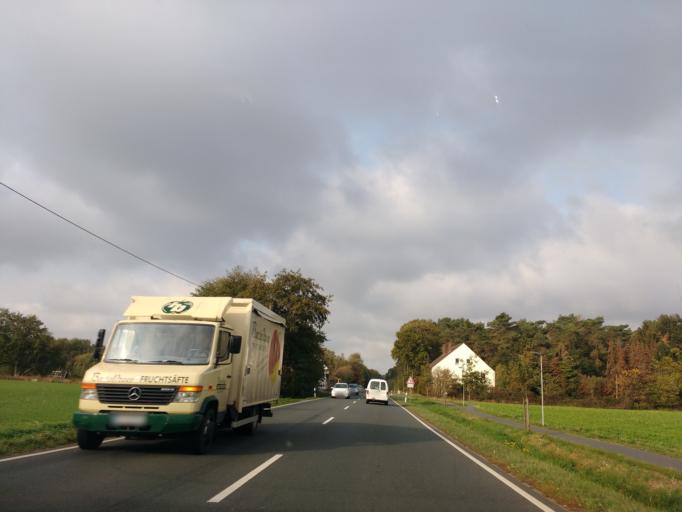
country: DE
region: North Rhine-Westphalia
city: Halle
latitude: 52.0351
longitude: 8.3586
